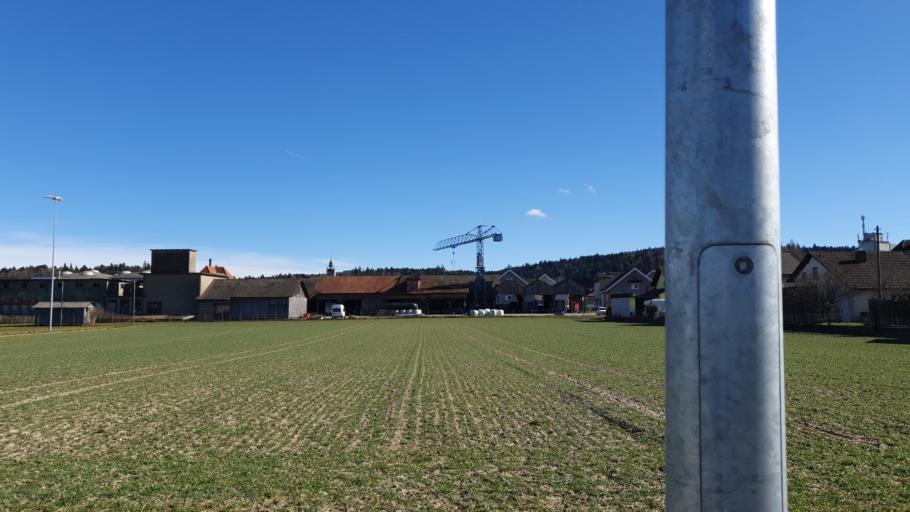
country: CH
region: Bern
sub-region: Oberaargau
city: Lotzwil
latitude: 47.1904
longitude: 7.7849
